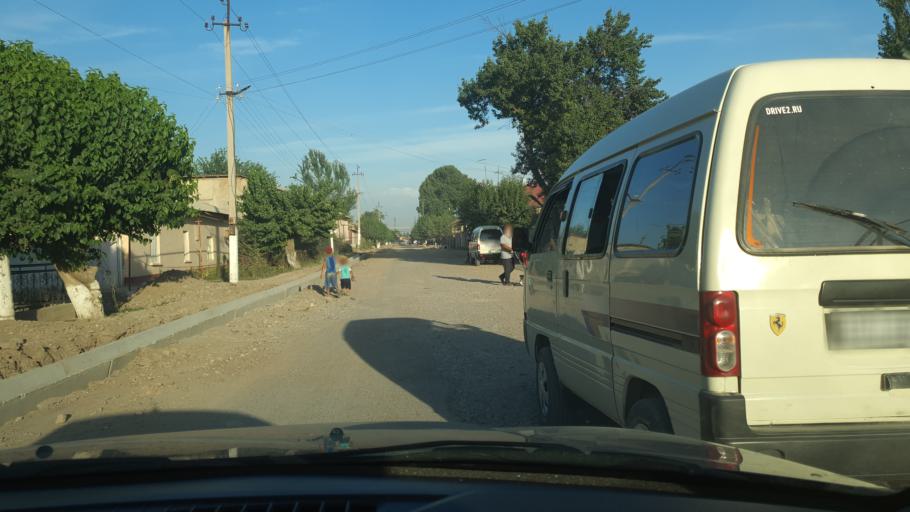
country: UZ
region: Toshkent
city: Tuytepa
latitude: 41.1043
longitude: 69.3985
